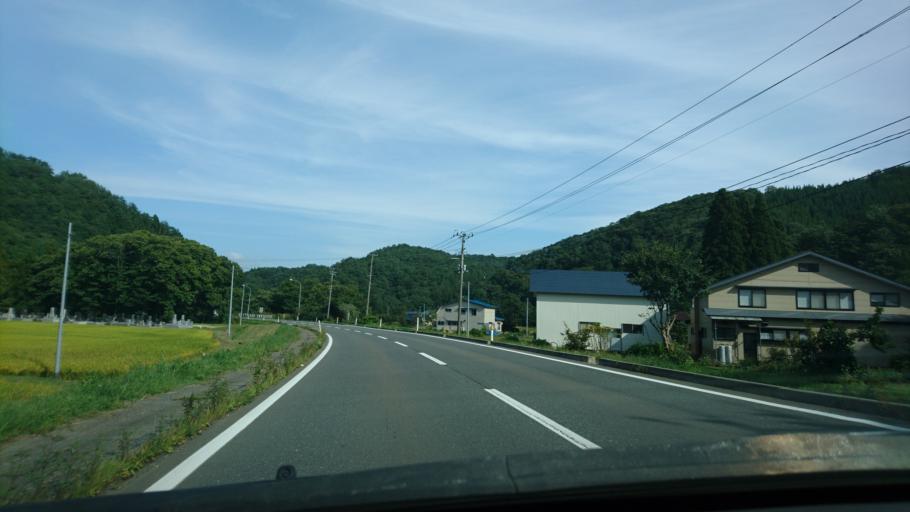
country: JP
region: Akita
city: Yokotemachi
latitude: 39.3106
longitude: 140.7619
